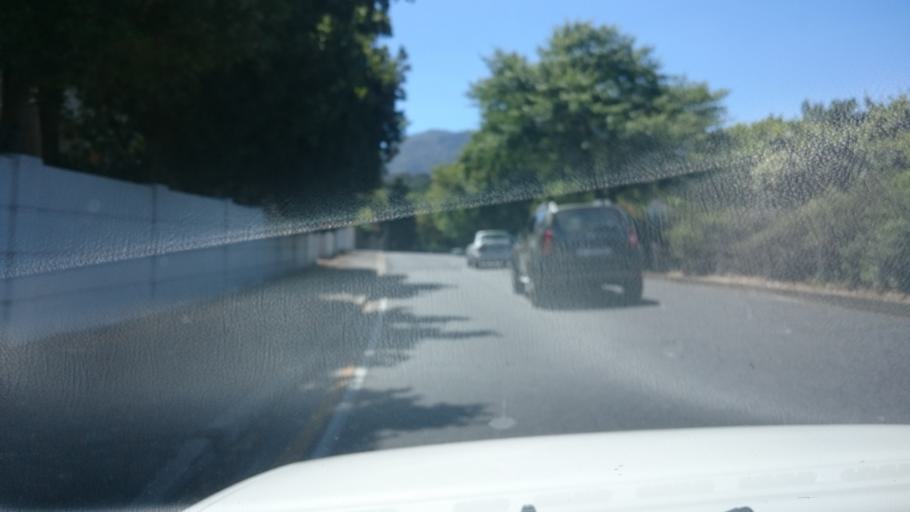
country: ZA
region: Western Cape
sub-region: City of Cape Town
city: Claremont
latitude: -34.0023
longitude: 18.4605
